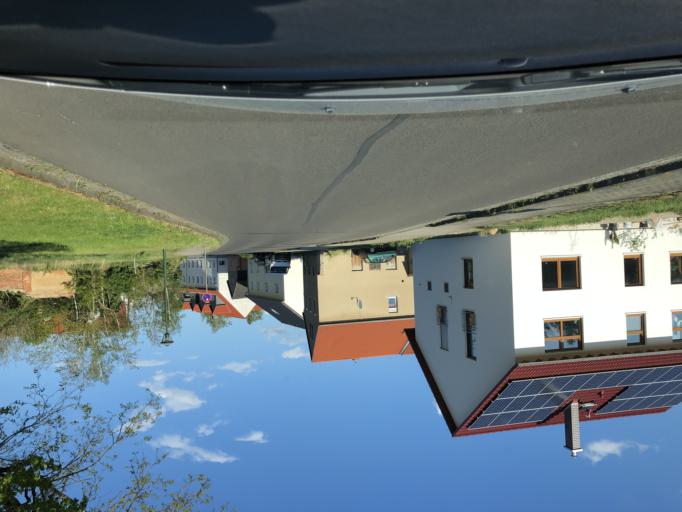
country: DE
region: Saxony
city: Lobstadt
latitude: 51.1338
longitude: 12.4464
